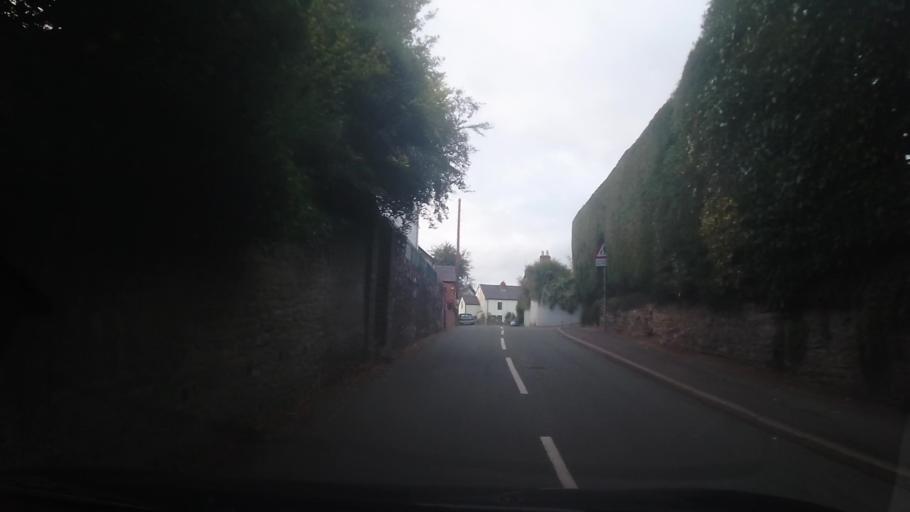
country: GB
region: England
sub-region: Shropshire
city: Bishop's Castle
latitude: 52.4957
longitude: -2.9972
